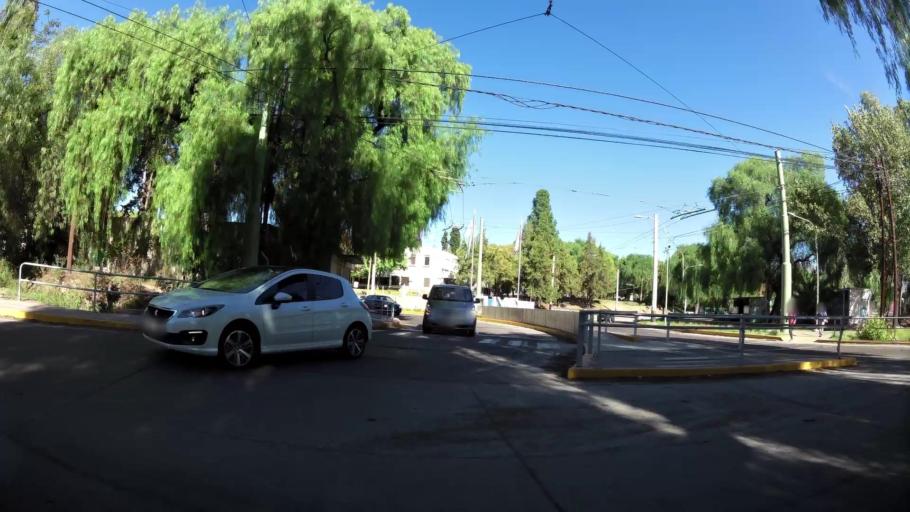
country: AR
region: Mendoza
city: Mendoza
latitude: -32.8817
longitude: -68.8737
